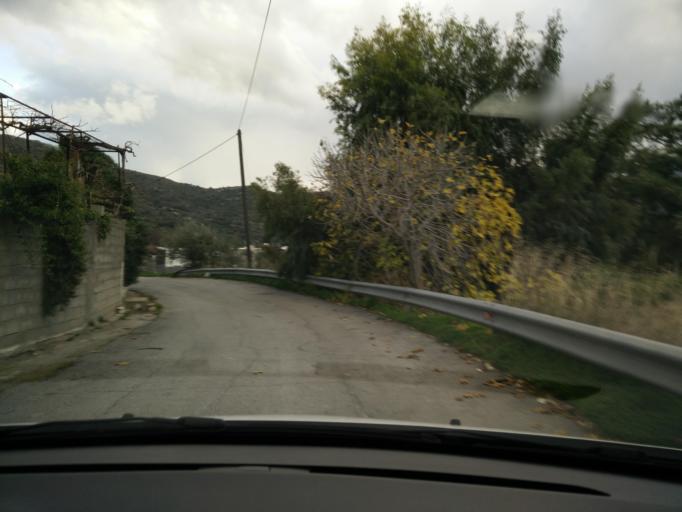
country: GR
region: Crete
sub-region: Nomos Lasithiou
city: Kritsa
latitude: 35.0949
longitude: 25.6872
